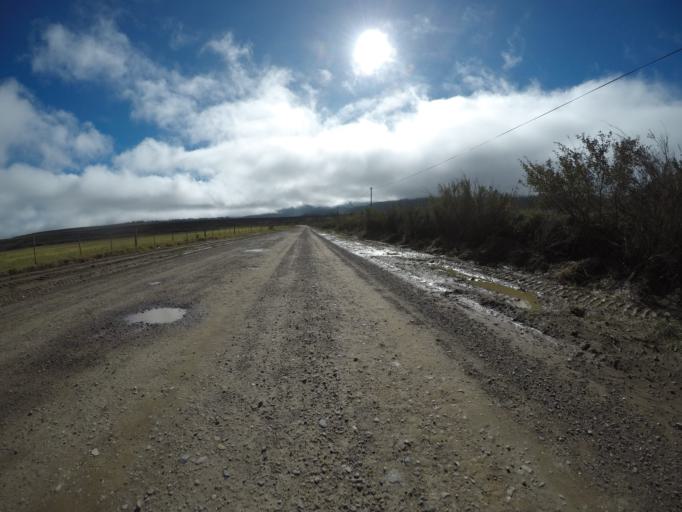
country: ZA
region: Western Cape
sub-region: Cape Winelands District Municipality
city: Ashton
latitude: -34.1246
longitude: 19.8394
